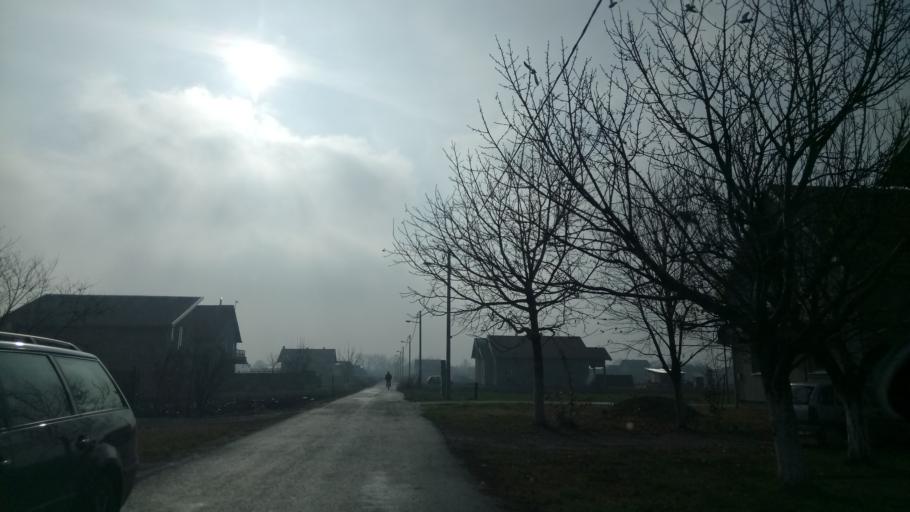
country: RS
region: Autonomna Pokrajina Vojvodina
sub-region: Sremski Okrug
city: Stara Pazova
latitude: 44.9800
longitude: 20.1745
